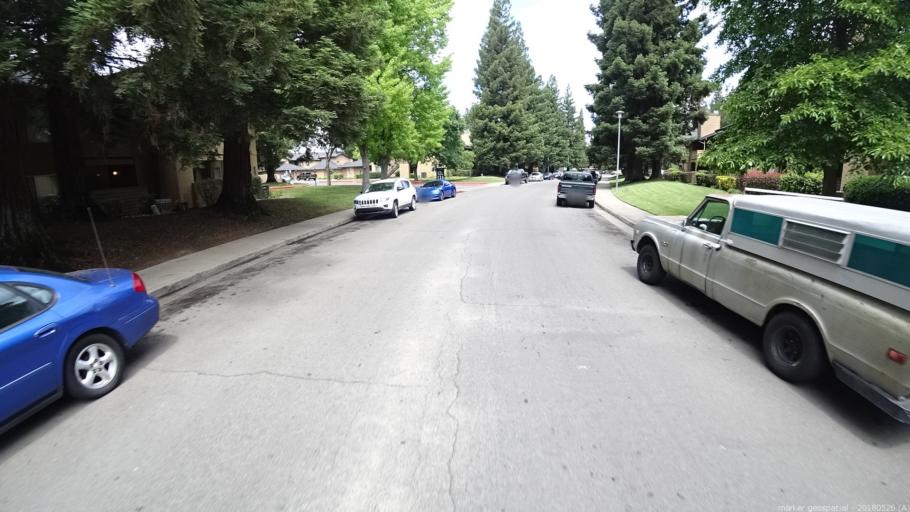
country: US
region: California
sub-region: Sacramento County
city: Sacramento
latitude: 38.6097
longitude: -121.4966
